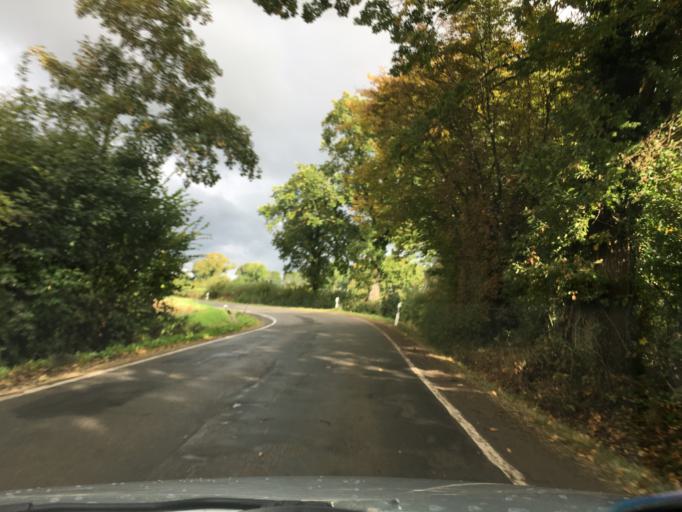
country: DE
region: Schleswig-Holstein
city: Gettorf
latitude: 54.3897
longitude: 9.9869
